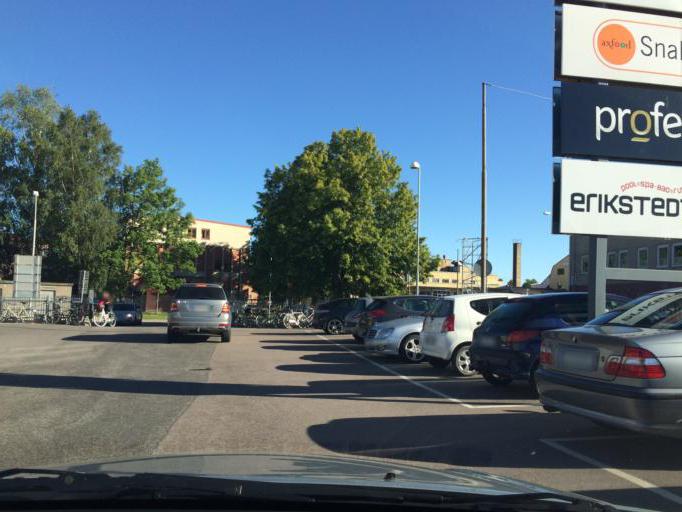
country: SE
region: Soedermanland
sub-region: Eskilstuna Kommun
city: Eskilstuna
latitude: 59.3775
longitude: 16.4981
